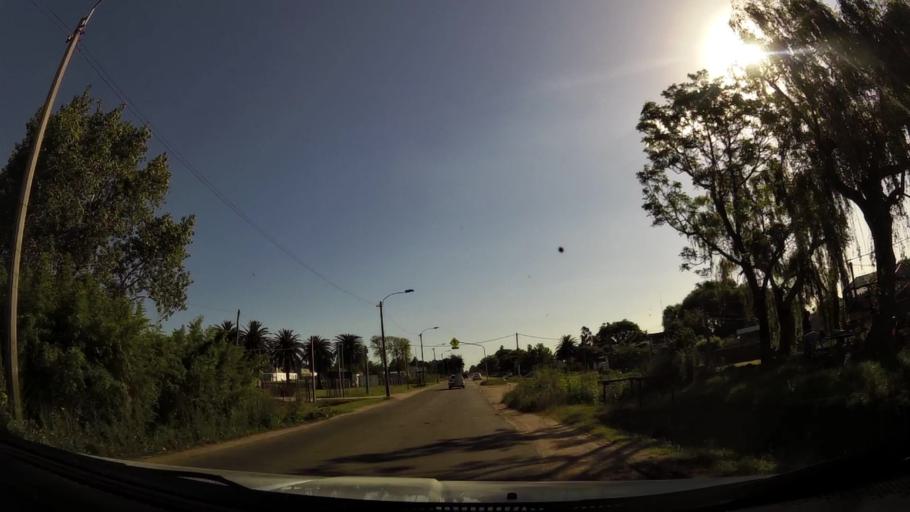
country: UY
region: Canelones
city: La Paz
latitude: -34.8162
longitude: -56.1720
